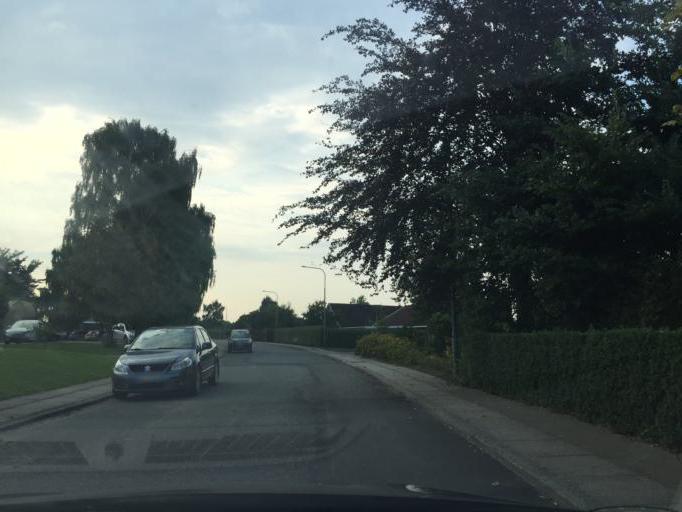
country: DK
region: South Denmark
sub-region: Kerteminde Kommune
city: Langeskov
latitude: 55.3104
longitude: 10.5904
